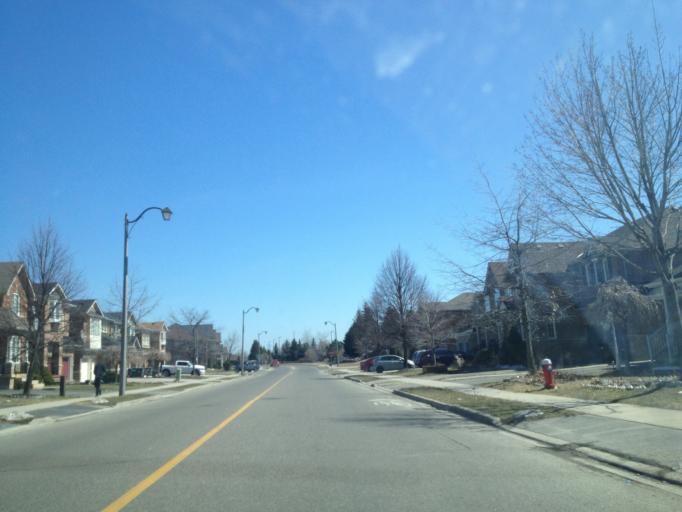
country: CA
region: Ontario
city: Brampton
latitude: 43.6858
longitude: -79.8162
